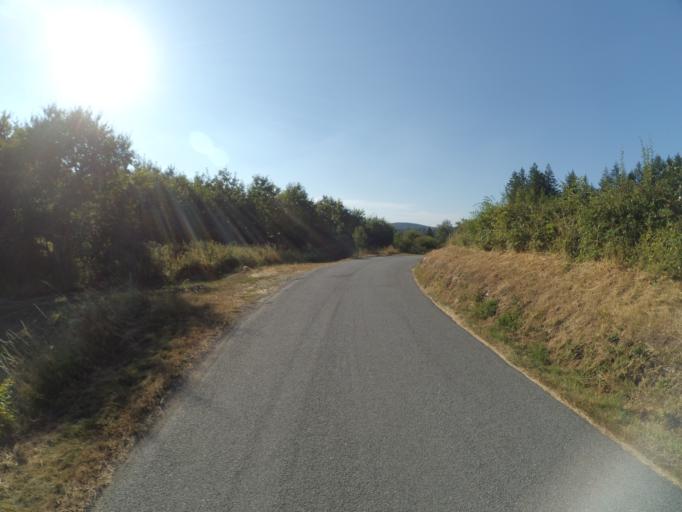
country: FR
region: Limousin
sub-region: Departement de la Correze
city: Bugeat
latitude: 45.7532
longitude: 1.9276
